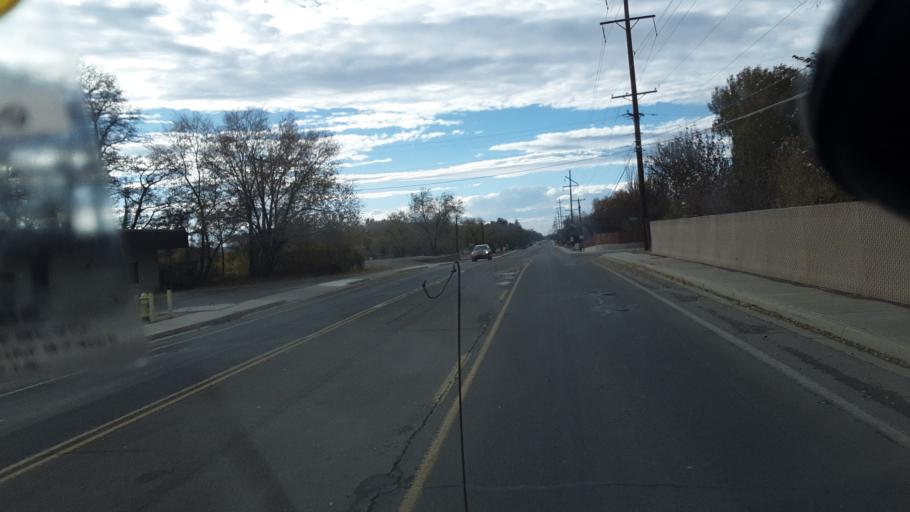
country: US
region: New Mexico
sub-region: San Juan County
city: Farmington
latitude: 36.7265
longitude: -108.1722
